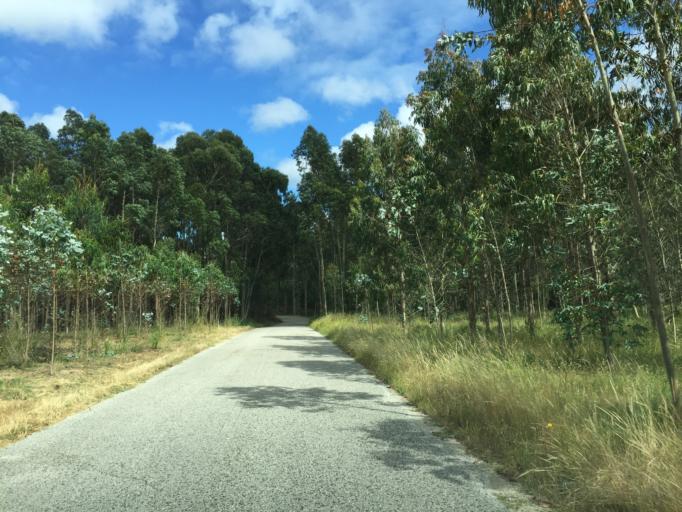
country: PT
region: Coimbra
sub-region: Figueira da Foz
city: Tavarede
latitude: 40.2115
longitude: -8.8412
